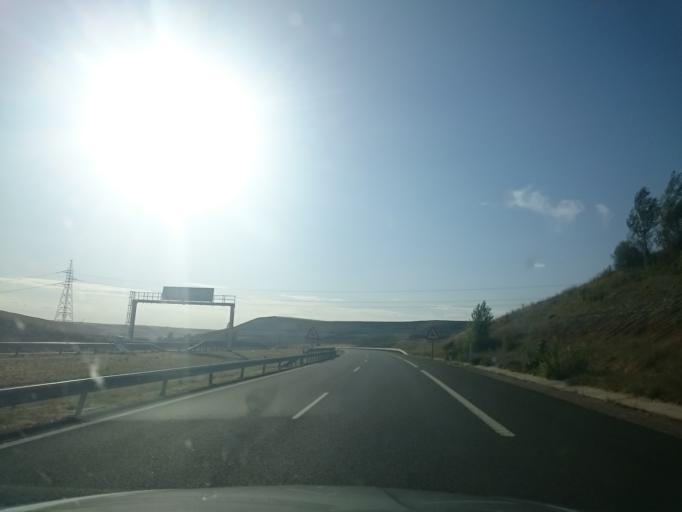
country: ES
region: Castille and Leon
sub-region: Provincia de Burgos
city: Tardajos
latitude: 42.3588
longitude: -3.8027
